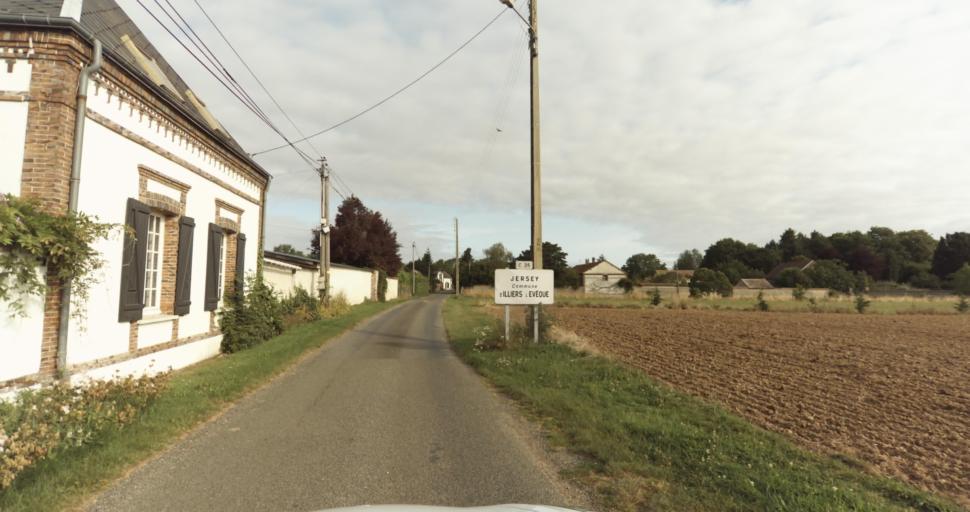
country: FR
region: Centre
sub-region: Departement d'Eure-et-Loir
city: Saint-Remy-sur-Avre
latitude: 48.8354
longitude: 1.2441
